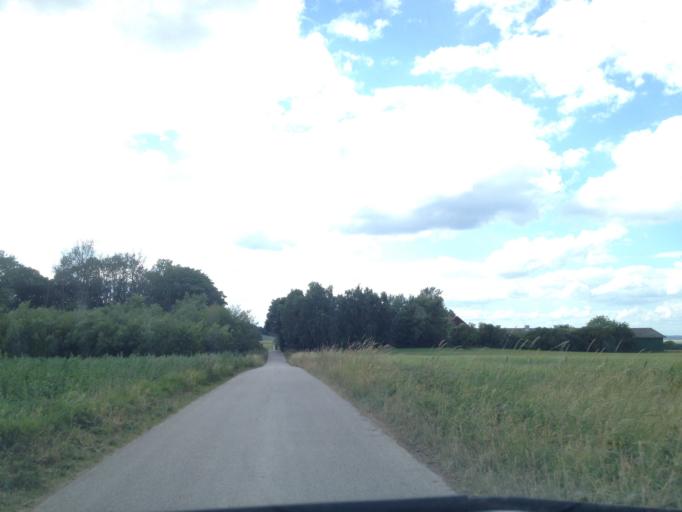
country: DK
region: Central Jutland
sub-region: Syddjurs Kommune
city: Ronde
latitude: 56.1970
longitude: 10.4984
